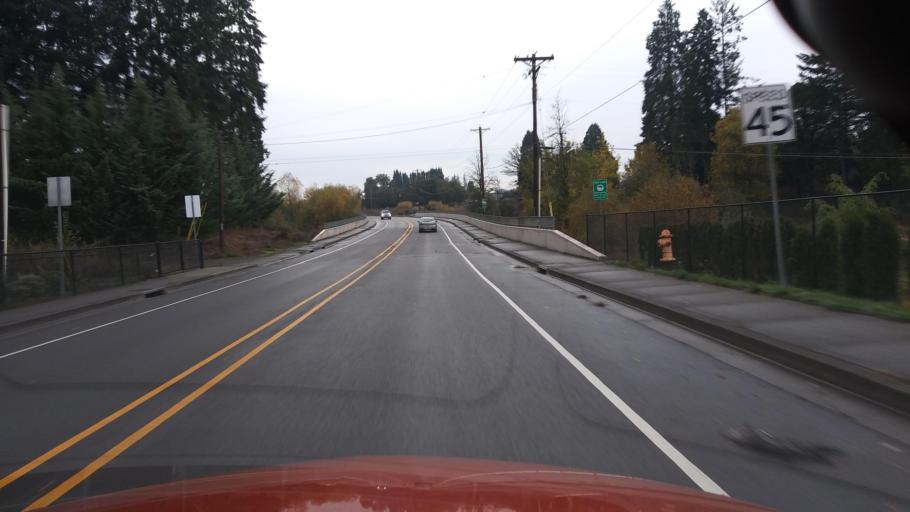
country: US
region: Oregon
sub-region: Washington County
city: Cornelius
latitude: 45.5279
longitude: -123.0592
